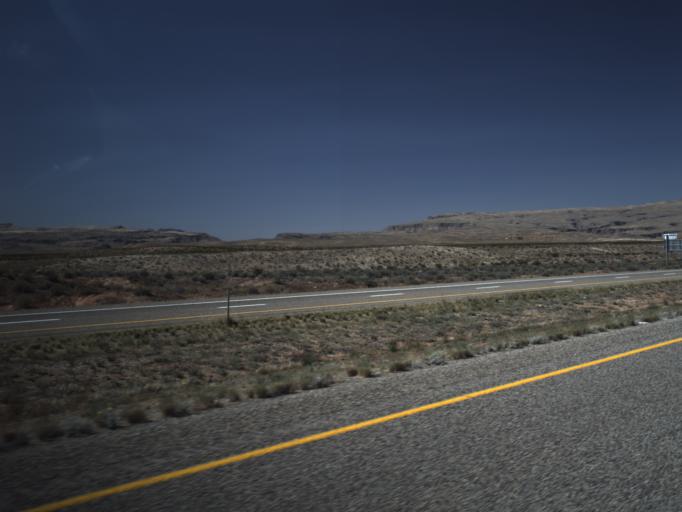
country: US
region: Utah
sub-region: Washington County
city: Saint George
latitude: 37.0027
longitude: -113.5797
